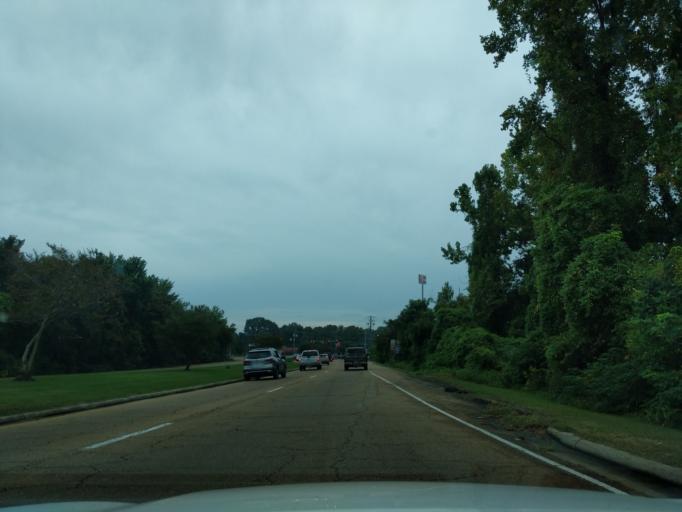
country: US
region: Mississippi
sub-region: Warren County
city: Vicksburg
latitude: 32.3166
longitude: -90.8771
